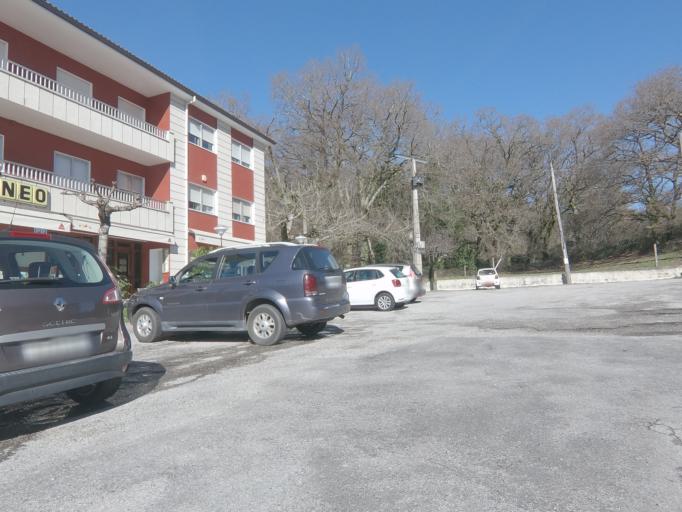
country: ES
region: Galicia
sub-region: Provincia de Ourense
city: Pinor
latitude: 42.5137
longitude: -8.0179
